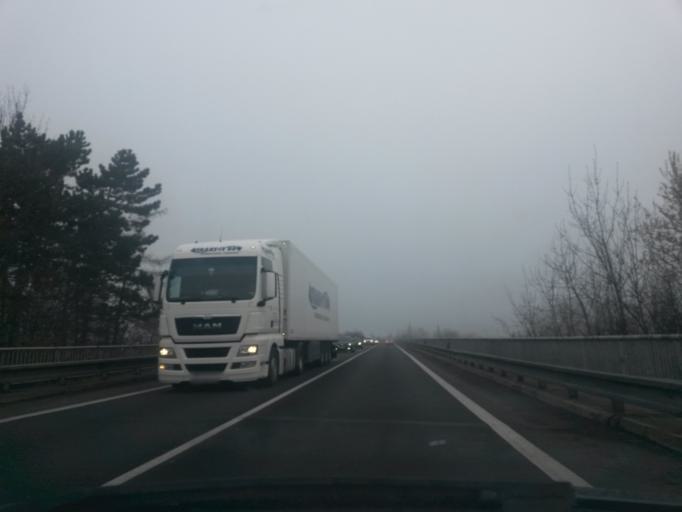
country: CZ
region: Ustecky
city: Cerncice
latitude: 50.3328
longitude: 13.8396
